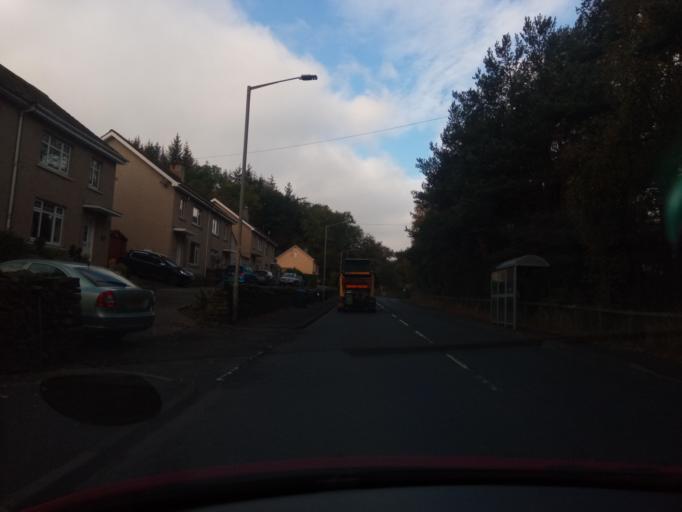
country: GB
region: Scotland
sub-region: The Scottish Borders
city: Galashiels
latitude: 55.6274
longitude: -2.8368
